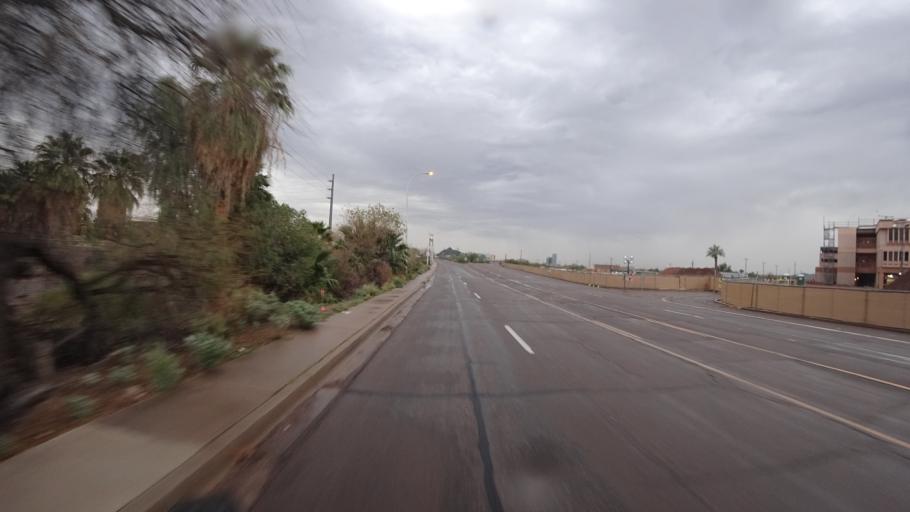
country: US
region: Arizona
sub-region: Maricopa County
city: Tempe Junction
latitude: 33.4470
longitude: -111.9505
